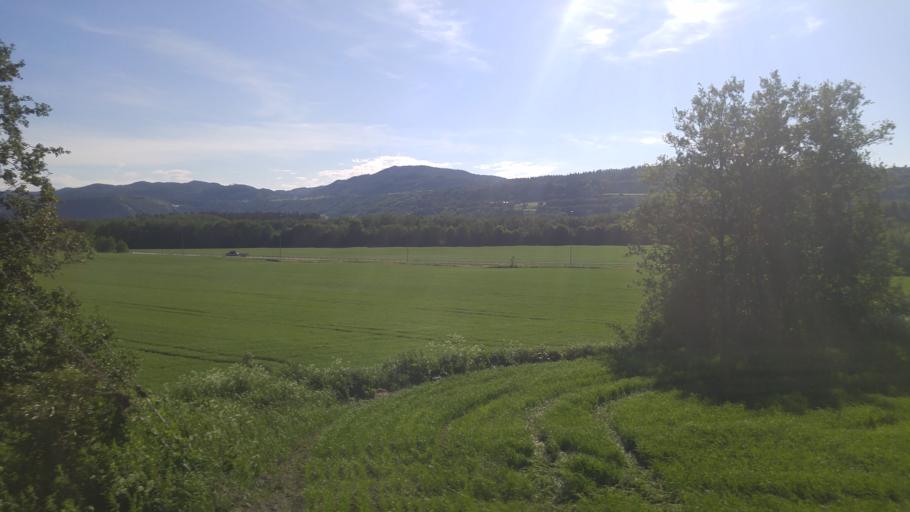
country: NO
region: Sor-Trondelag
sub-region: Melhus
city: Melhus
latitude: 63.2745
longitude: 10.2896
